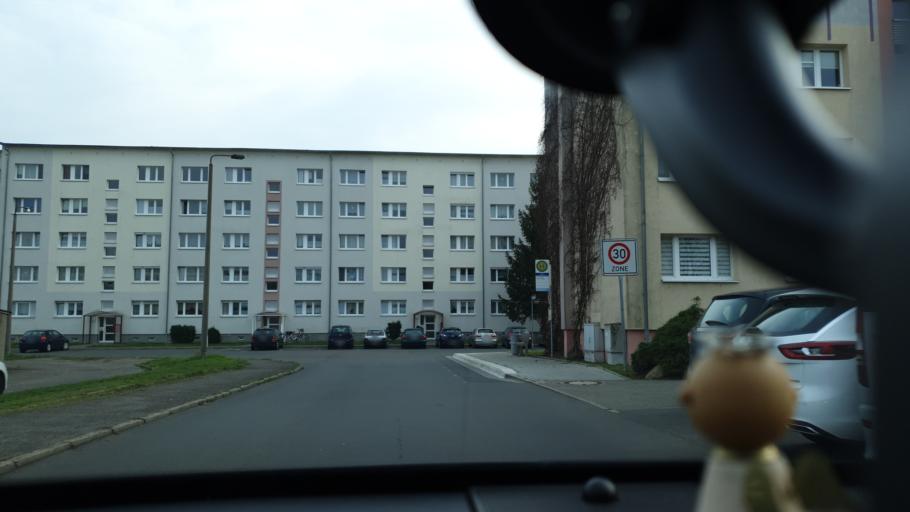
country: DE
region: Saxony
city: Torgau
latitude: 51.5532
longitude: 12.9823
